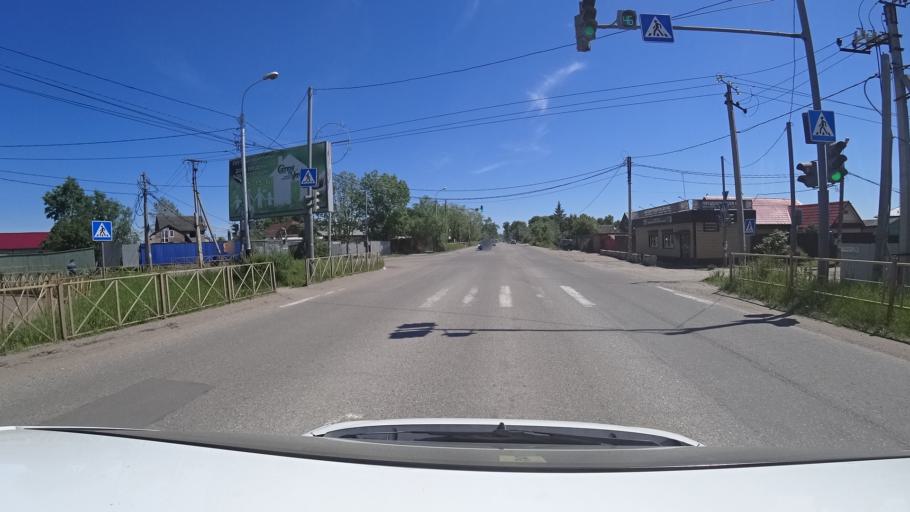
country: RU
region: Khabarovsk Krai
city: Topolevo
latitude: 48.4704
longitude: 135.1780
